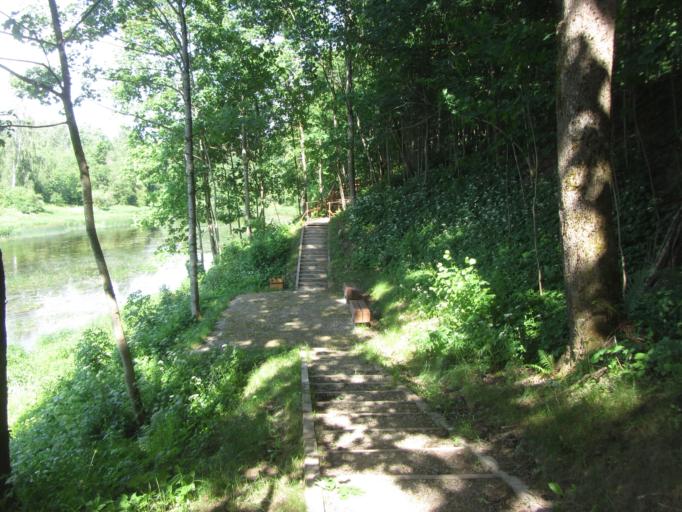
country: LT
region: Panevezys
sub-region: Birzai
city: Birzai
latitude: 56.3858
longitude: 24.7021
